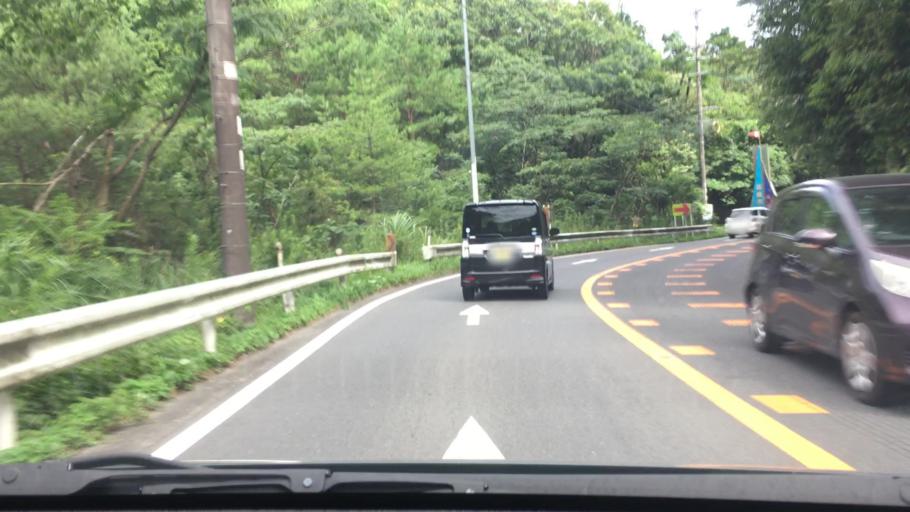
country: JP
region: Nagasaki
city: Togitsu
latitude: 32.9616
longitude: 129.7831
